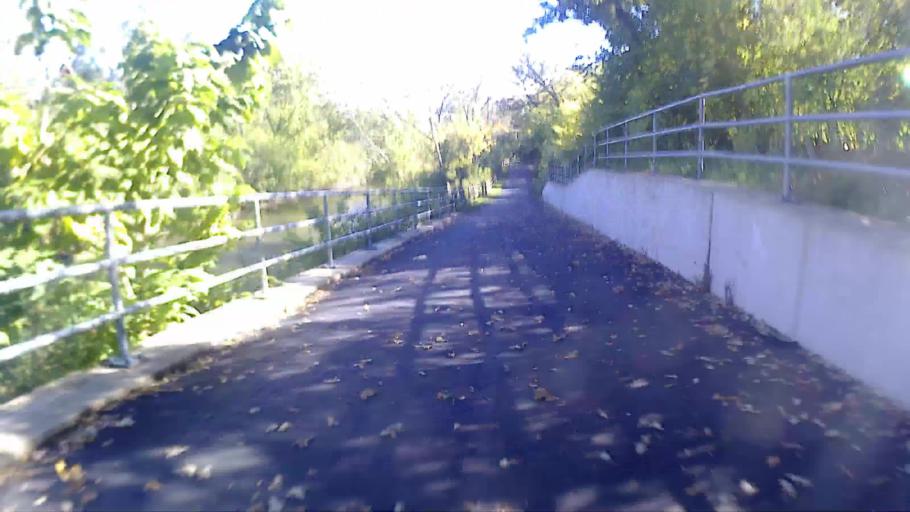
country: US
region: Illinois
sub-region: DuPage County
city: Villa Park
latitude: 41.9047
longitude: -87.9678
